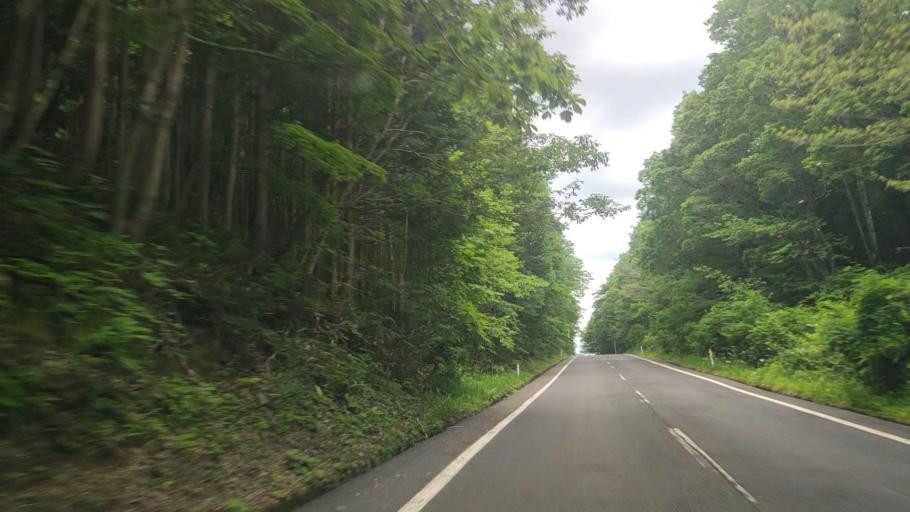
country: JP
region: Tottori
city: Kurayoshi
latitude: 35.2983
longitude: 133.9903
